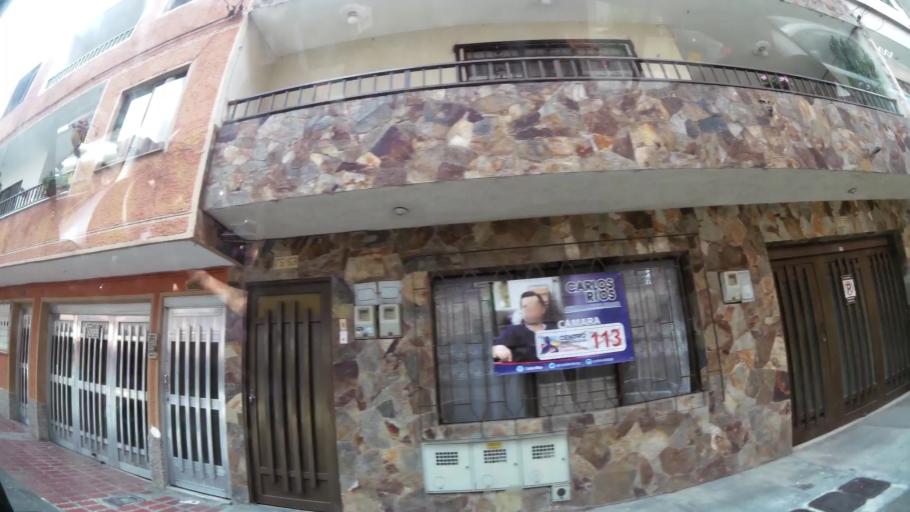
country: CO
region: Antioquia
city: Sabaneta
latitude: 6.1505
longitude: -75.6202
